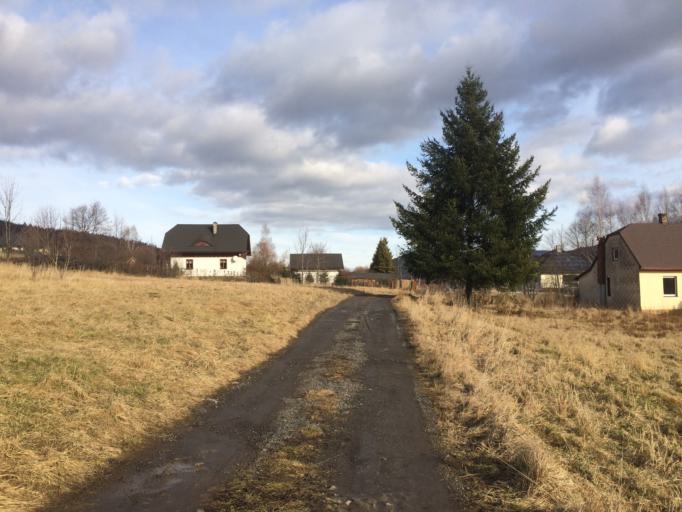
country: PL
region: Silesian Voivodeship
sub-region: Powiat bielski
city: Bystra
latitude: 49.7546
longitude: 19.0658
